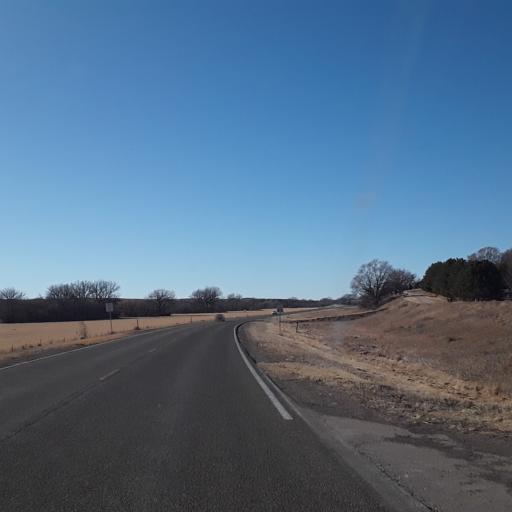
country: US
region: Nebraska
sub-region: Frontier County
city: Stockville
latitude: 40.6285
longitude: -100.5284
